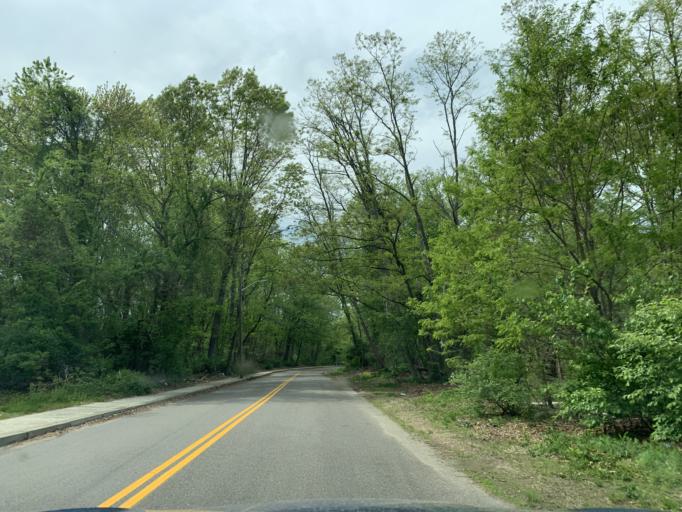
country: US
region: Rhode Island
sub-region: Providence County
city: Cranston
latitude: 41.7735
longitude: -71.4745
